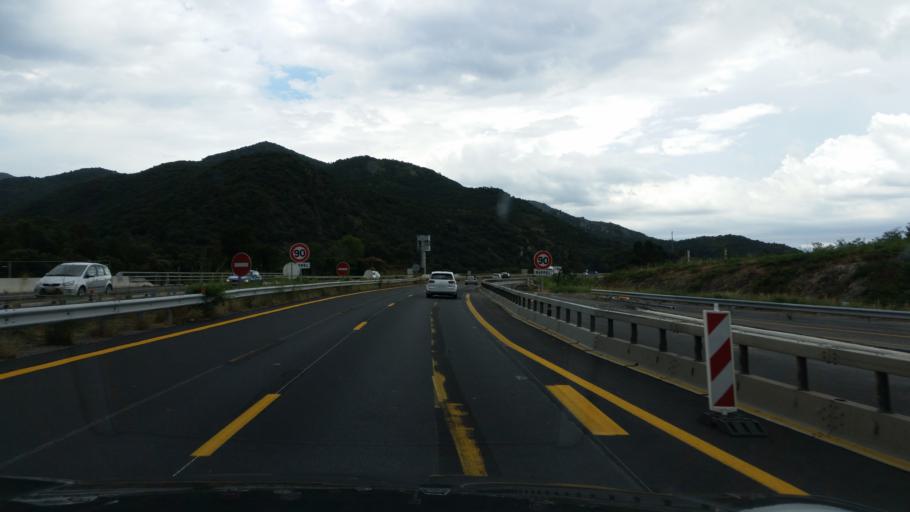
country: FR
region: Languedoc-Roussillon
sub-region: Departement des Pyrenees-Orientales
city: Montesquiu d'Albera
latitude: 42.4723
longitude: 2.8624
